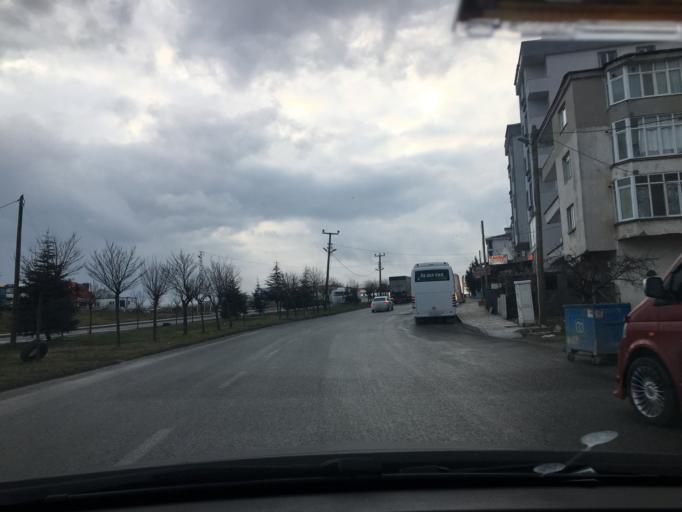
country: TR
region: Tekirdag
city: Cerkezkoey
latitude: 41.2790
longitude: 27.9868
